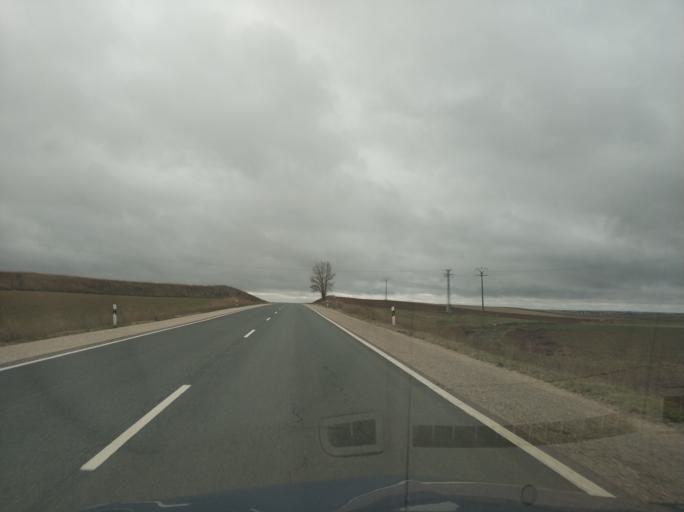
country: ES
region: Castille and Leon
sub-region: Provincia de Salamanca
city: Pajares de la Laguna
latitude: 41.0819
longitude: -5.5194
